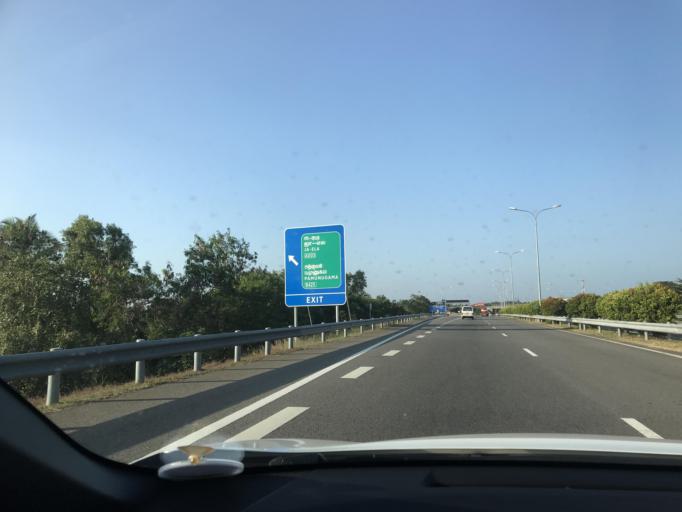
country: LK
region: Western
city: Ja Ela
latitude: 7.0770
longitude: 79.8775
